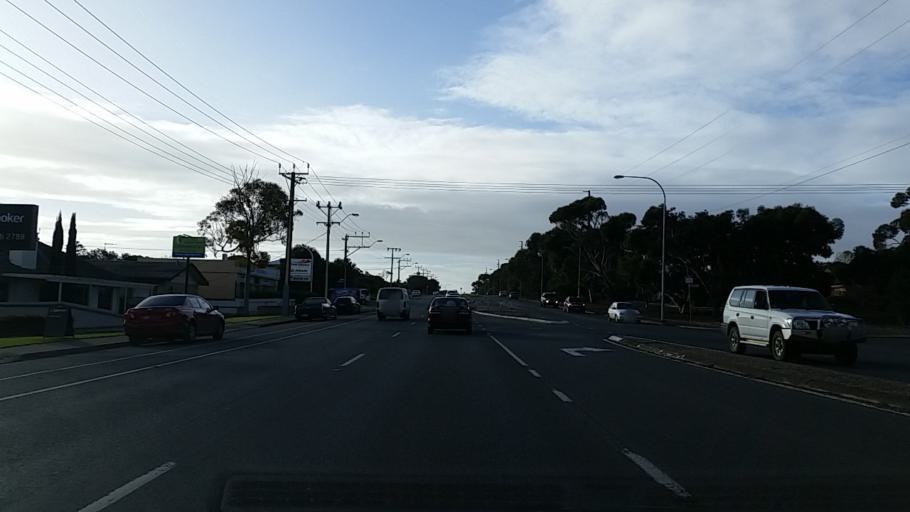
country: AU
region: South Australia
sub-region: Adelaide
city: Port Noarlunga
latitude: -35.1359
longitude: 138.4860
